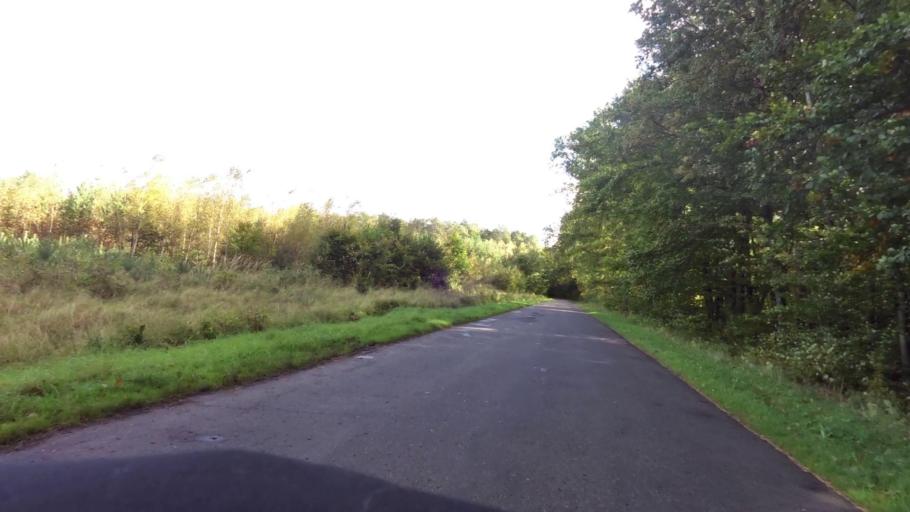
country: PL
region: West Pomeranian Voivodeship
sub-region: Powiat bialogardzki
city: Bialogard
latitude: 53.9937
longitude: 16.0924
